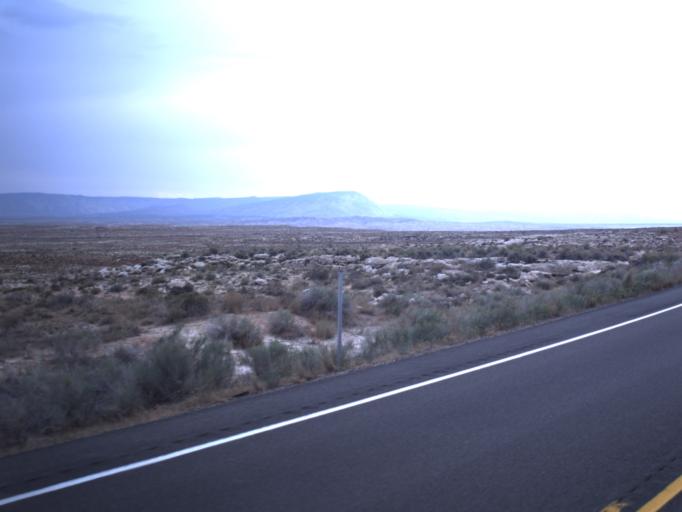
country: US
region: Utah
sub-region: Uintah County
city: Naples
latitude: 40.2627
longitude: -109.4492
